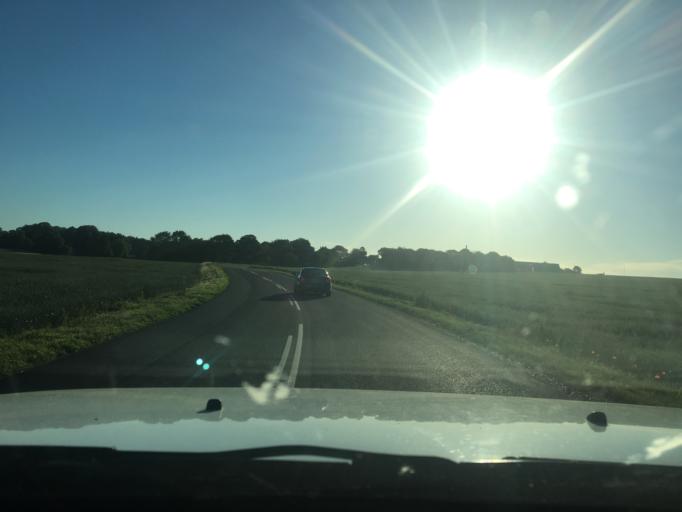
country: DK
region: Central Jutland
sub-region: Randers Kommune
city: Langa
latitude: 56.3907
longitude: 9.9454
